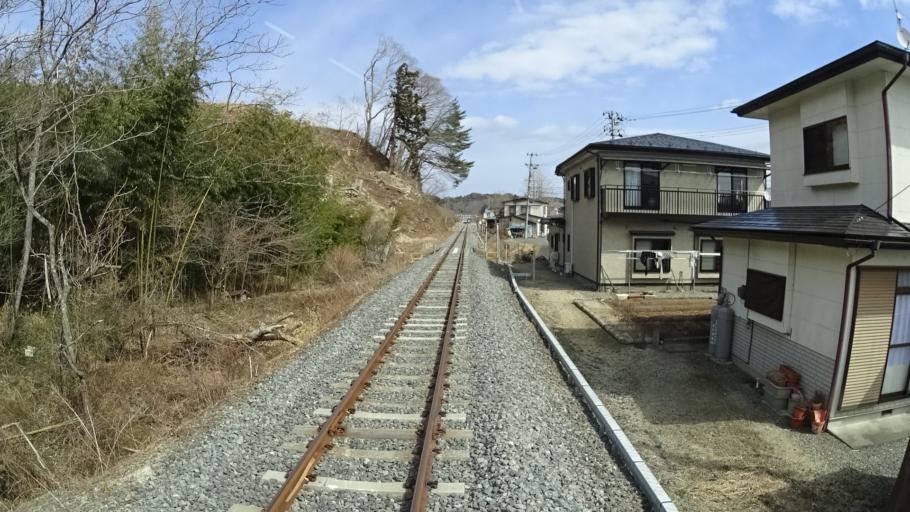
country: JP
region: Iwate
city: Miyako
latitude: 39.5734
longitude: 141.9335
